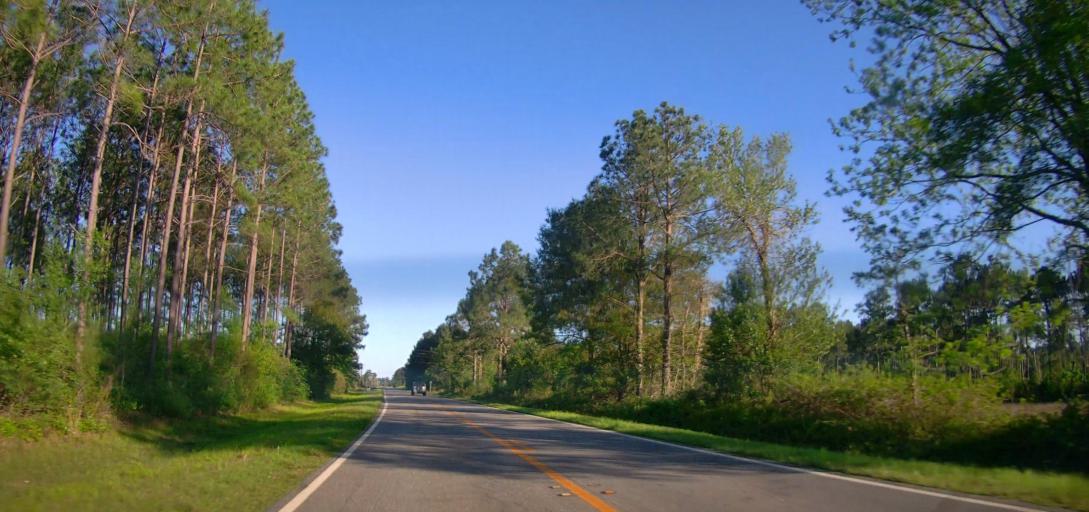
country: US
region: Georgia
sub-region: Ben Hill County
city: Fitzgerald
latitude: 31.6710
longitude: -83.1903
